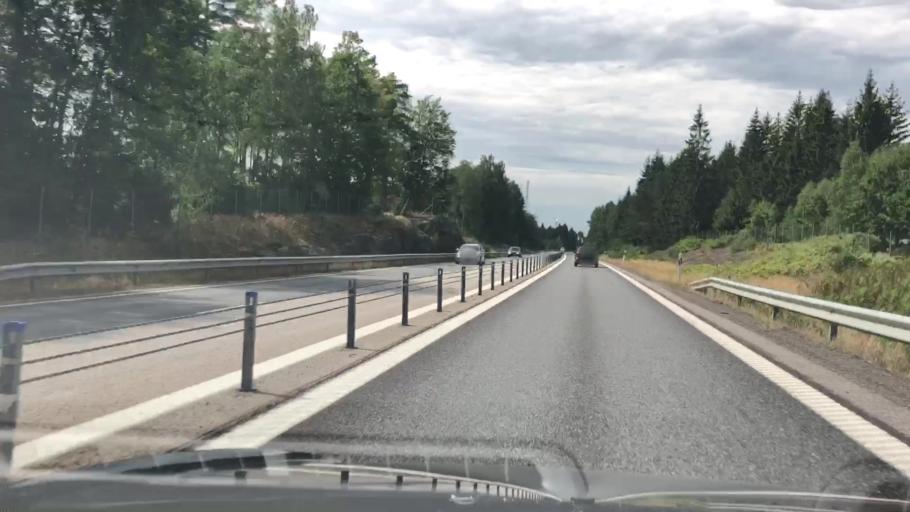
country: SE
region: Blekinge
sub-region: Ronneby Kommun
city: Ronneby
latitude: 56.2257
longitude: 15.2238
